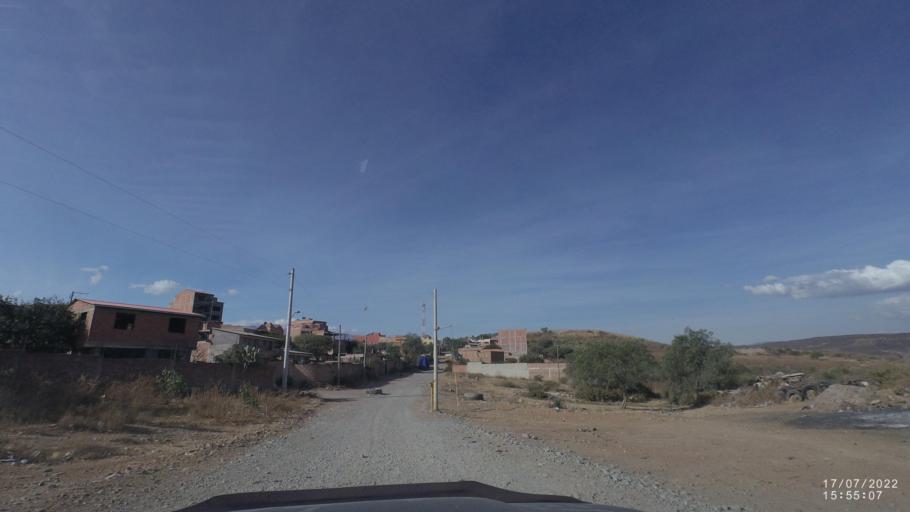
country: BO
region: Cochabamba
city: Sipe Sipe
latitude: -17.4250
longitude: -66.2885
